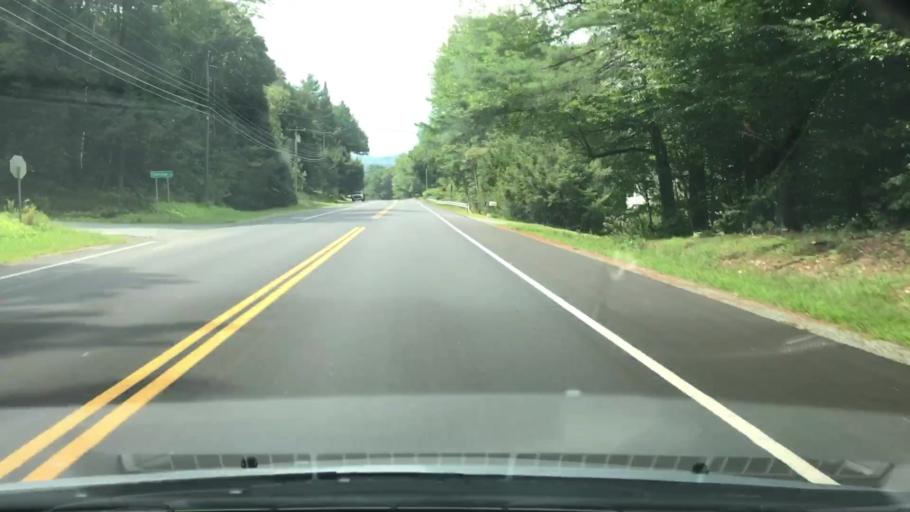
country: US
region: New Hampshire
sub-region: Grafton County
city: Lyme
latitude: 43.7499
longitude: -72.2173
